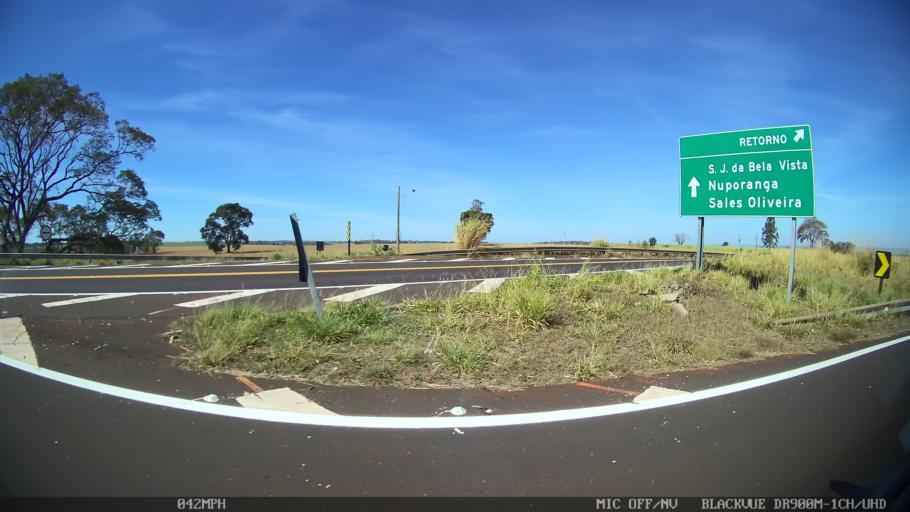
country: BR
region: Sao Paulo
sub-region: Nuporanga
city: Nuporanga
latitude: -20.5621
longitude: -47.6259
